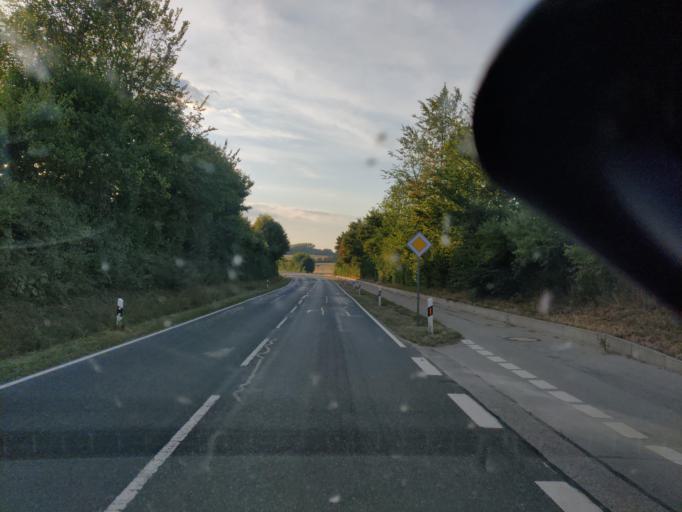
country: DE
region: Bavaria
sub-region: Regierungsbezirk Mittelfranken
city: Hilpoltstein
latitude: 49.1649
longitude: 11.2462
